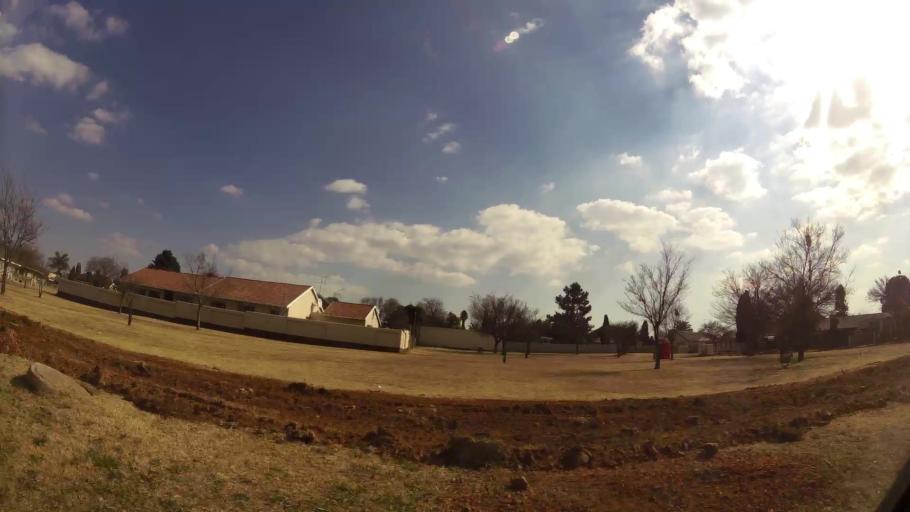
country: ZA
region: Gauteng
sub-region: Ekurhuleni Metropolitan Municipality
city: Germiston
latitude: -26.1795
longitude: 28.1983
